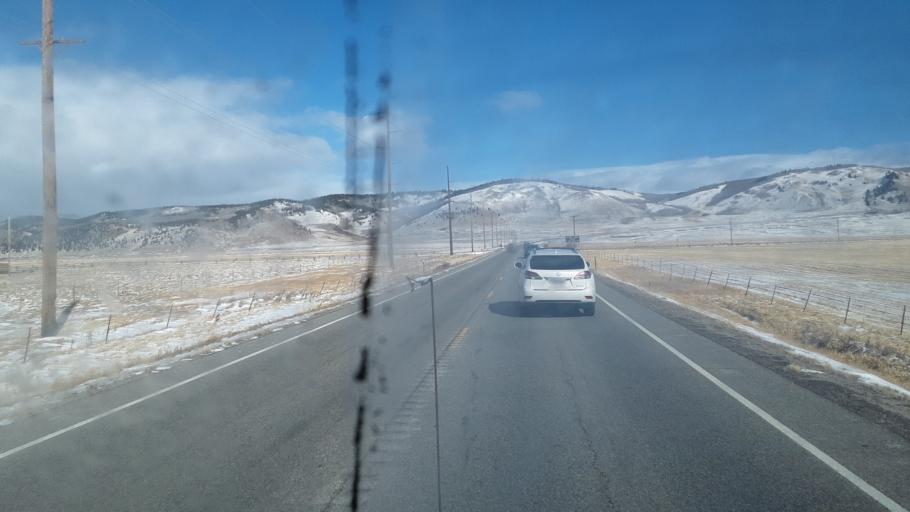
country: US
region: Colorado
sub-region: Summit County
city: Breckenridge
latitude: 39.3896
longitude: -105.7881
